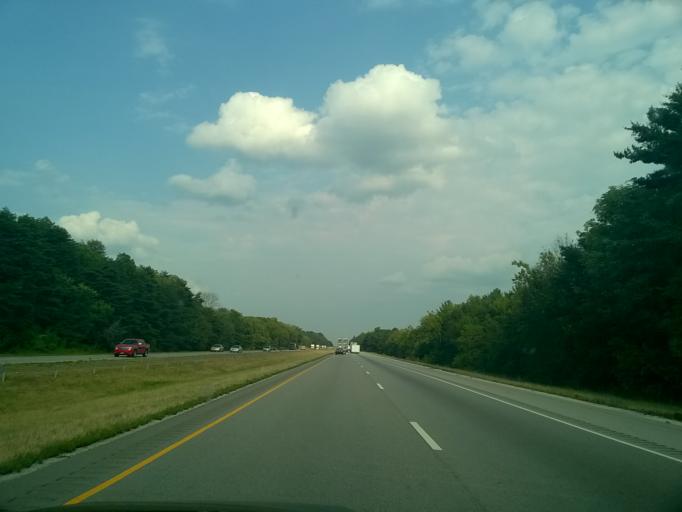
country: US
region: Indiana
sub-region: Vigo County
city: Seelyville
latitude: 39.4510
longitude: -87.1886
